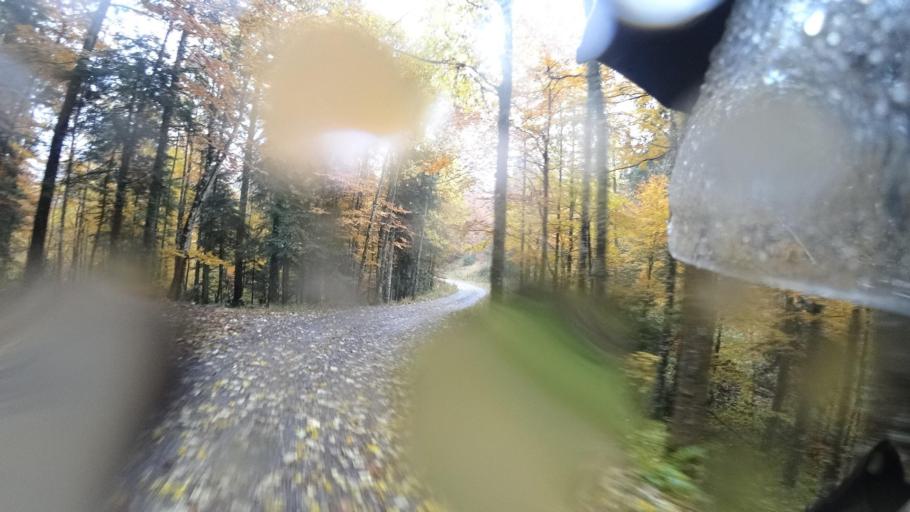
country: HR
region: Primorsko-Goranska
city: Vrbovsko
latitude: 45.3054
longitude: 15.0623
